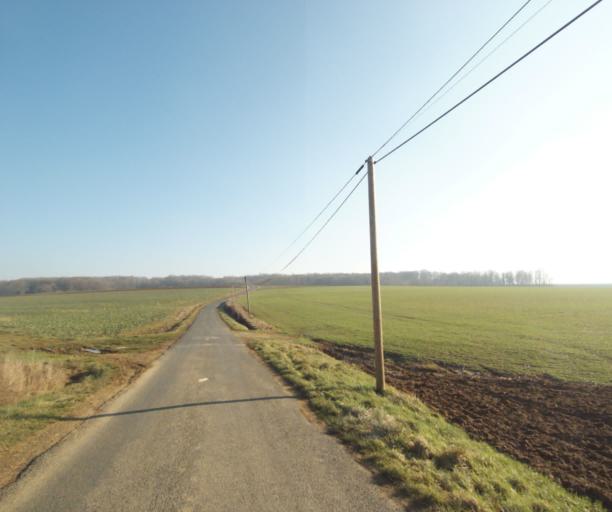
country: FR
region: Champagne-Ardenne
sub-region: Departement de la Haute-Marne
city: Wassy
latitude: 48.5099
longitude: 5.0179
